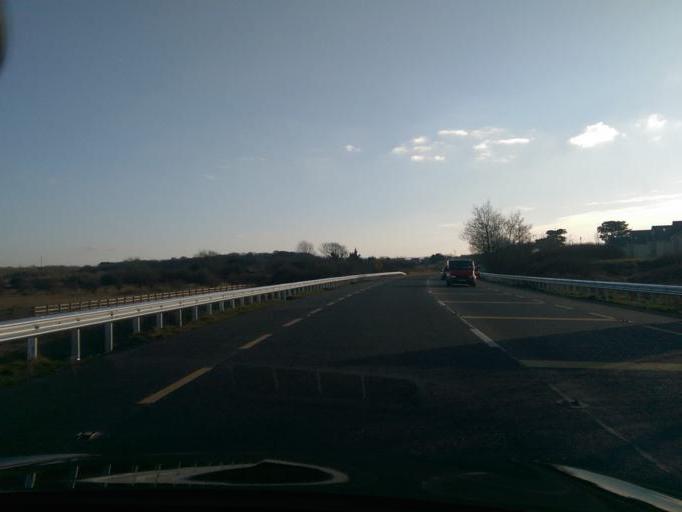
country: IE
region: Connaught
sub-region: County Galway
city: Oranmore
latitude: 53.2693
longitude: -8.9188
